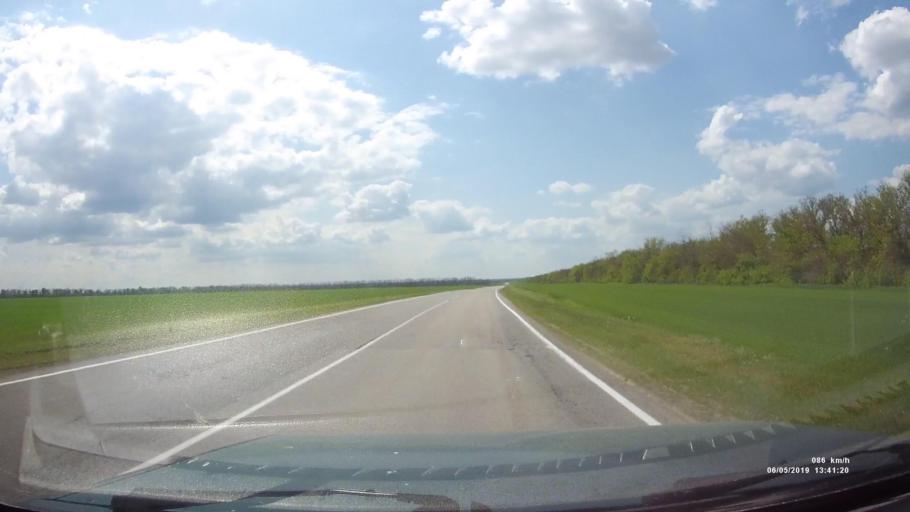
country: RU
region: Rostov
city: Ust'-Donetskiy
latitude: 47.6624
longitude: 40.6778
